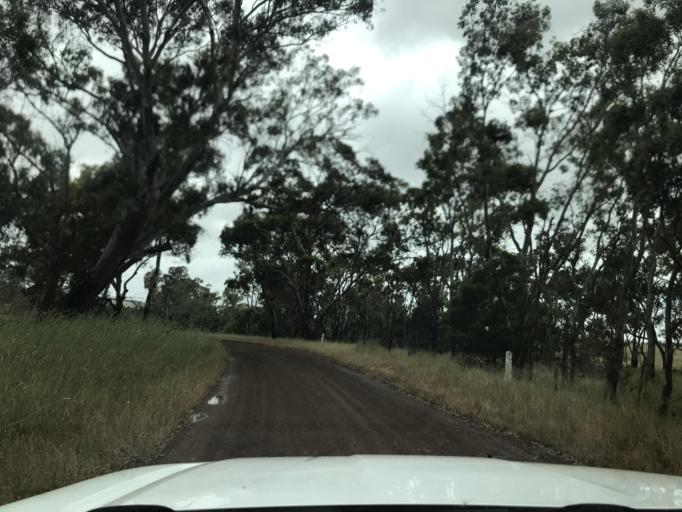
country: AU
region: South Australia
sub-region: Wattle Range
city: Penola
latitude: -37.2345
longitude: 141.4559
